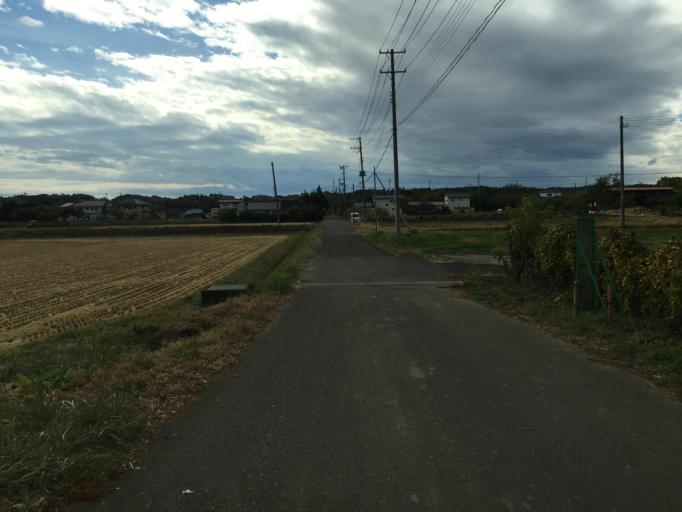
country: JP
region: Fukushima
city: Nihommatsu
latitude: 37.6552
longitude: 140.4525
